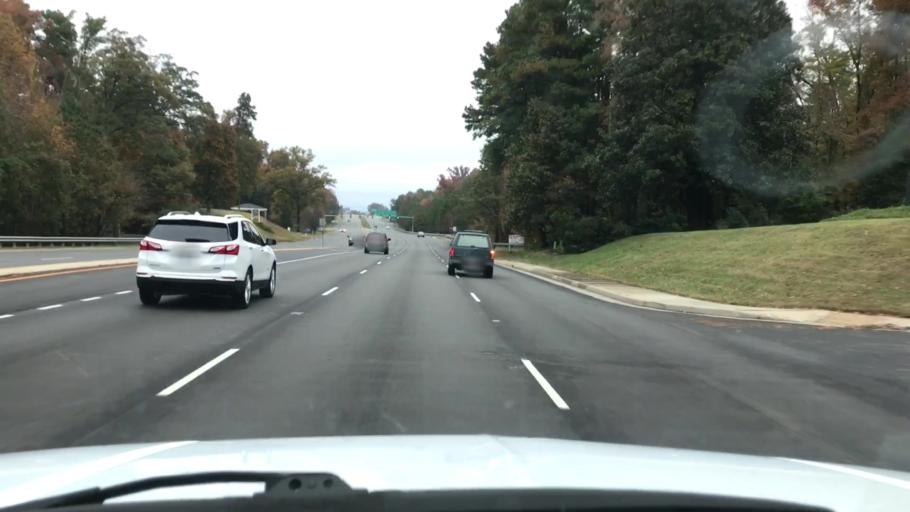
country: US
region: Virginia
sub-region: Henrico County
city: Chamberlayne
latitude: 37.6497
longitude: -77.4597
